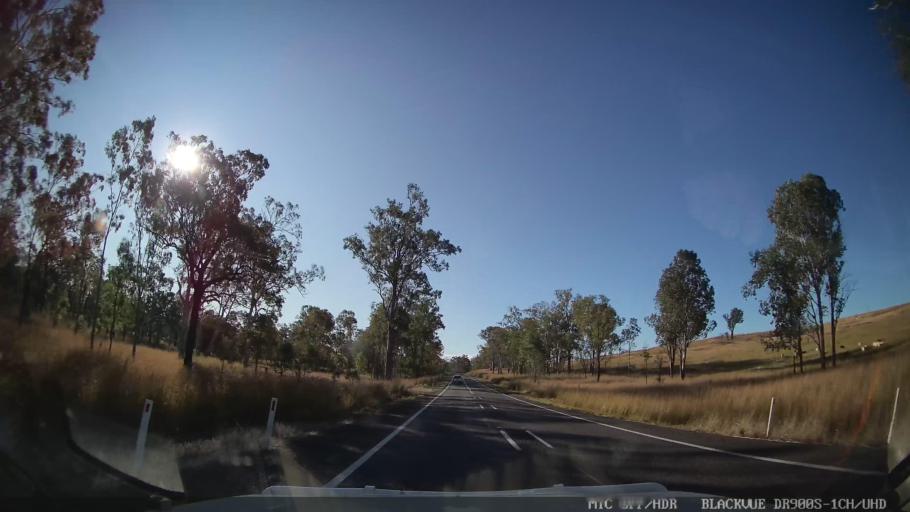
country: AU
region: Queensland
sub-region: Bundaberg
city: Sharon
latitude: -24.8332
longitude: 151.7093
